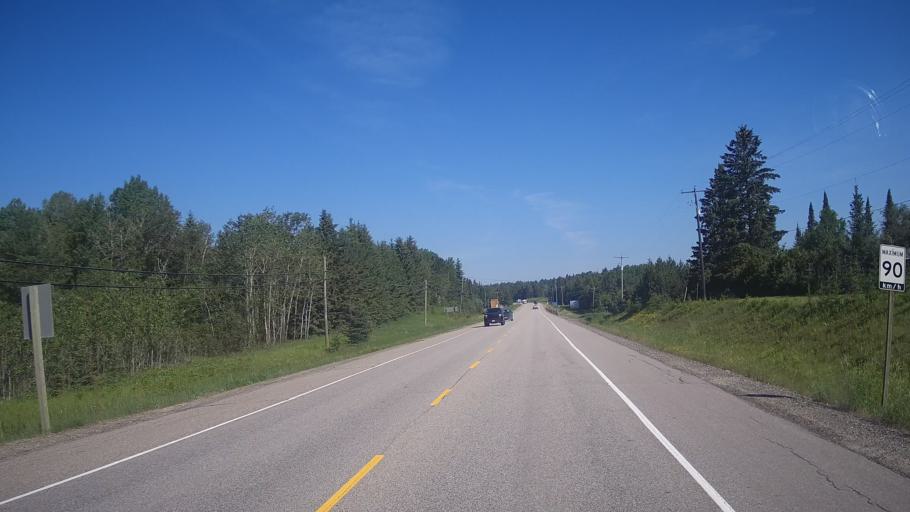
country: CA
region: Ontario
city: Dryden
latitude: 49.7780
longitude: -92.6960
